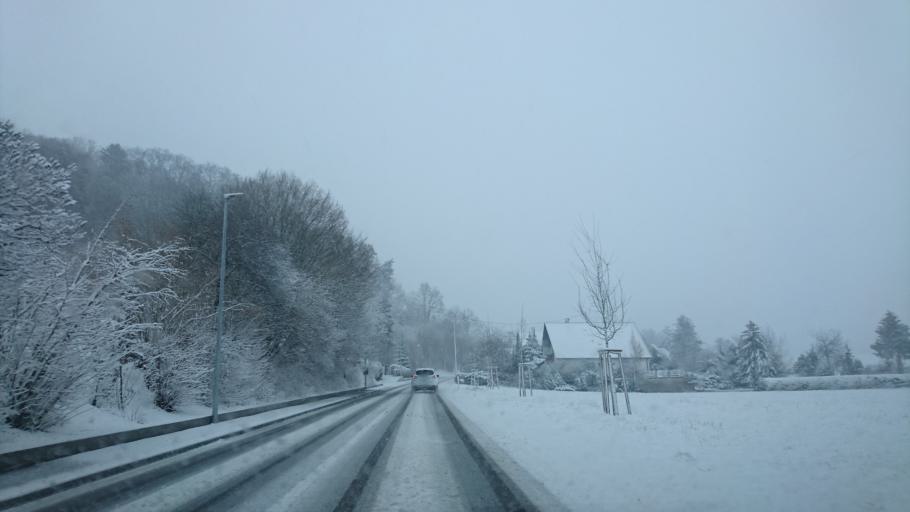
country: DE
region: Bavaria
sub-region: Swabia
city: Emersacker
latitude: 48.5078
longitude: 10.6802
